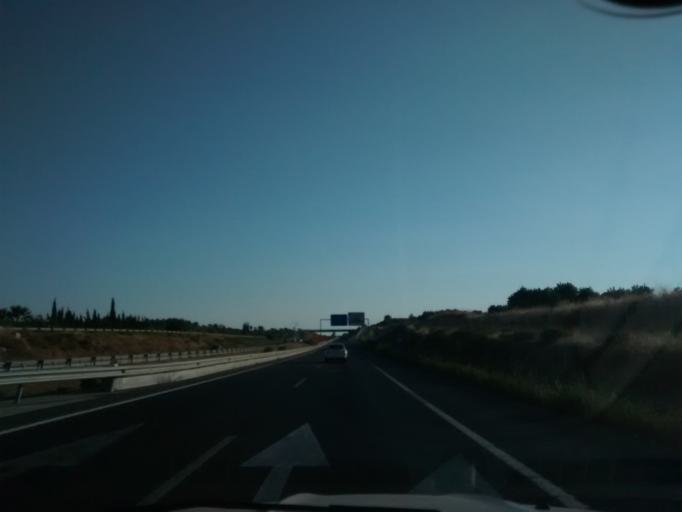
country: ES
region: Balearic Islands
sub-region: Illes Balears
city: Inca
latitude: 39.7396
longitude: 2.9450
